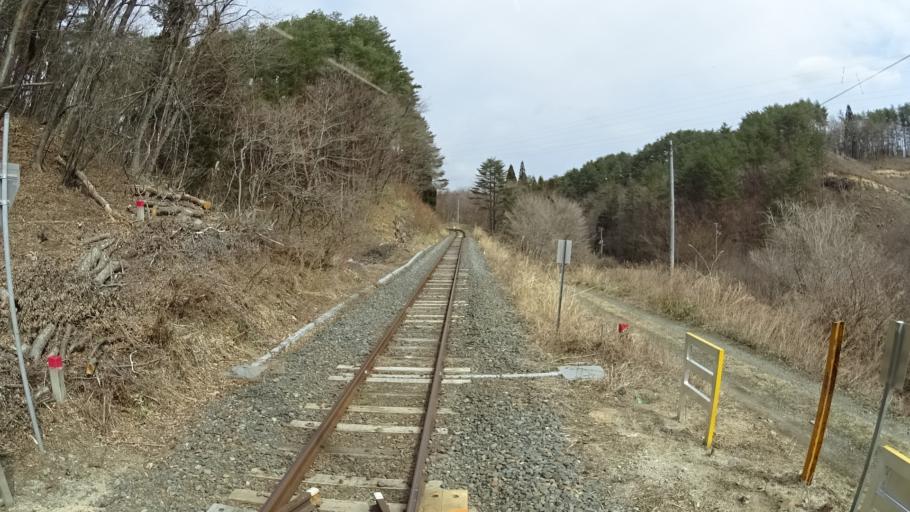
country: JP
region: Iwate
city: Yamada
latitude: 39.4982
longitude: 141.9294
